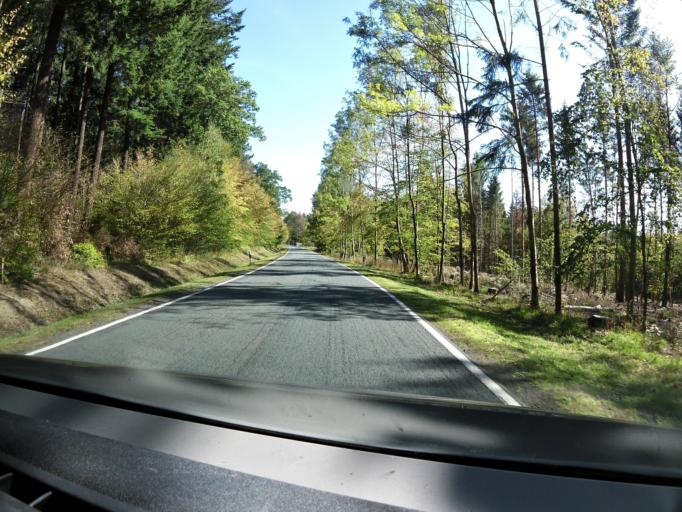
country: DE
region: Saxony-Anhalt
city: Hasselfelde
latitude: 51.6791
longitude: 10.9413
